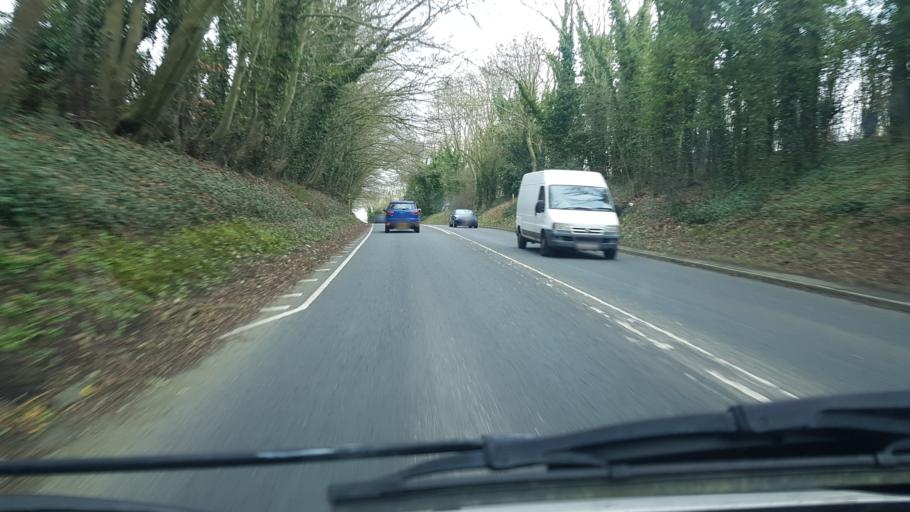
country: GB
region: England
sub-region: Wiltshire
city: Fyfield
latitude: 51.4162
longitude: -1.7953
